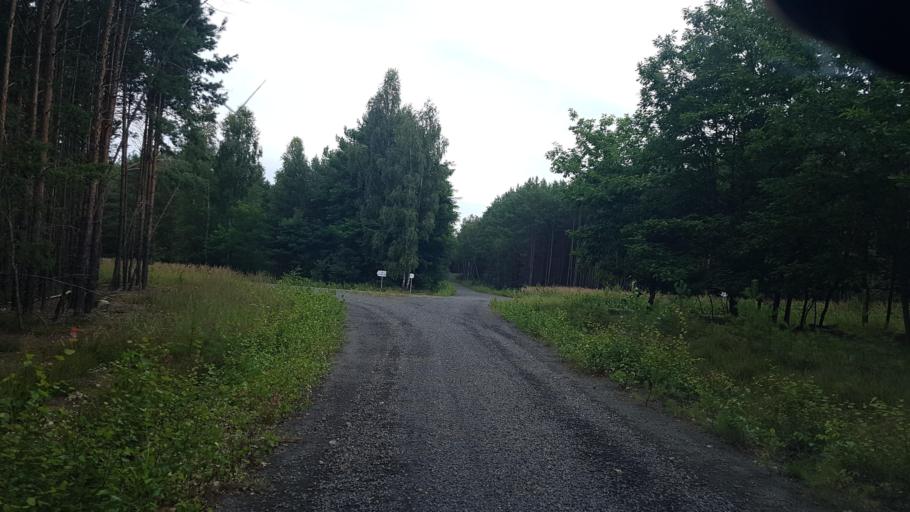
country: DE
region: Brandenburg
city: Grossraschen
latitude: 51.6272
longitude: 13.9894
